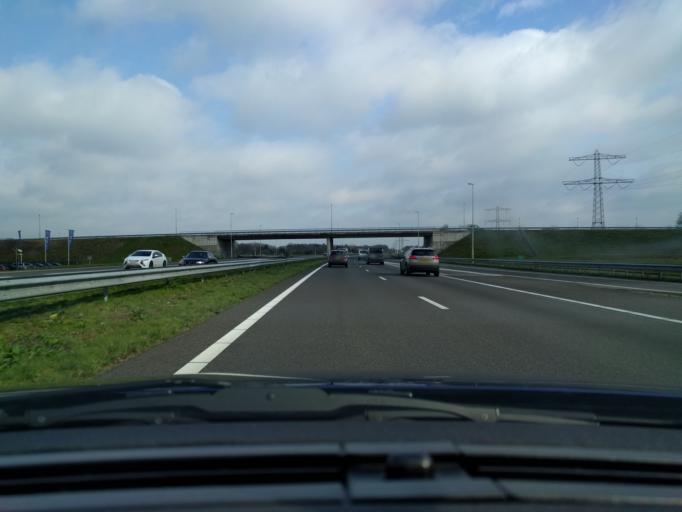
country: NL
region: North Brabant
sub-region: Gemeente Bernheze
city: Heesch
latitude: 51.7141
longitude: 5.5691
